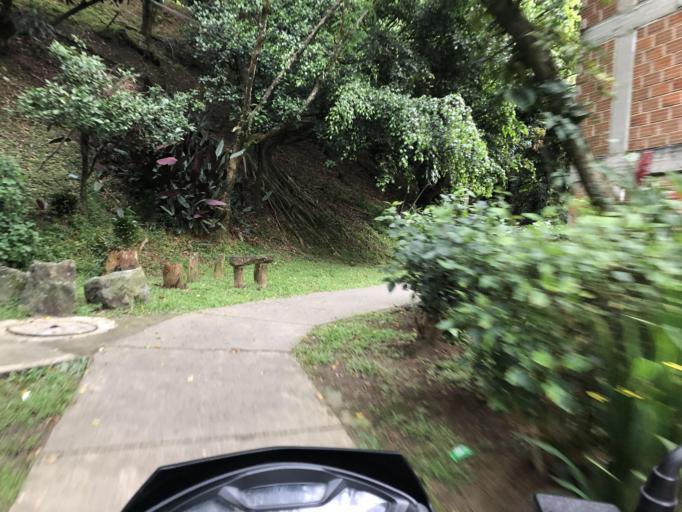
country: CO
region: Antioquia
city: Medellin
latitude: 6.2926
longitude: -75.5657
